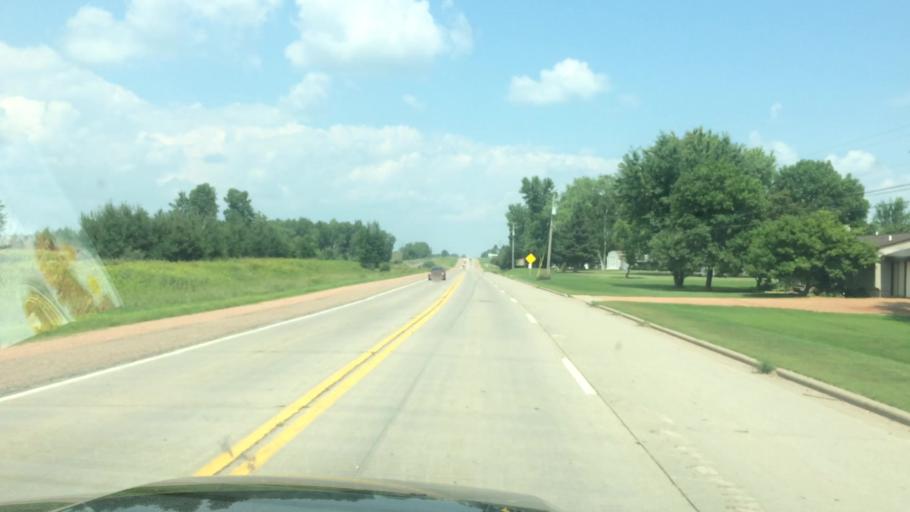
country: US
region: Wisconsin
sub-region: Clark County
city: Colby
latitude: 44.8547
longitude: -90.3159
